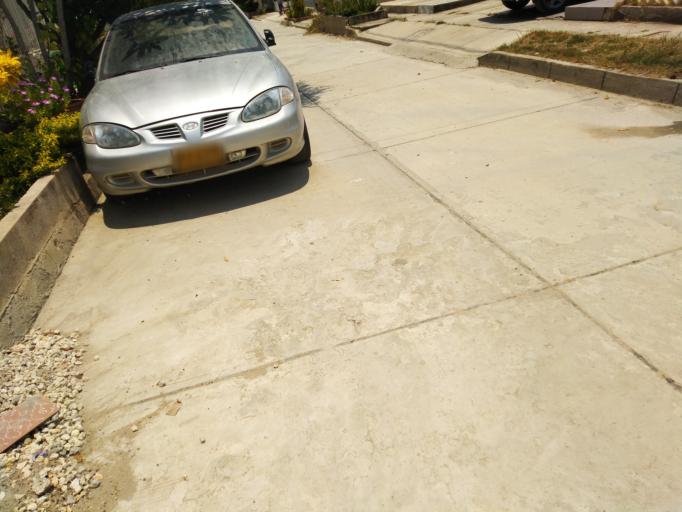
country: CO
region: Bolivar
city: Turbaco
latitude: 10.3091
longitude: -75.4040
